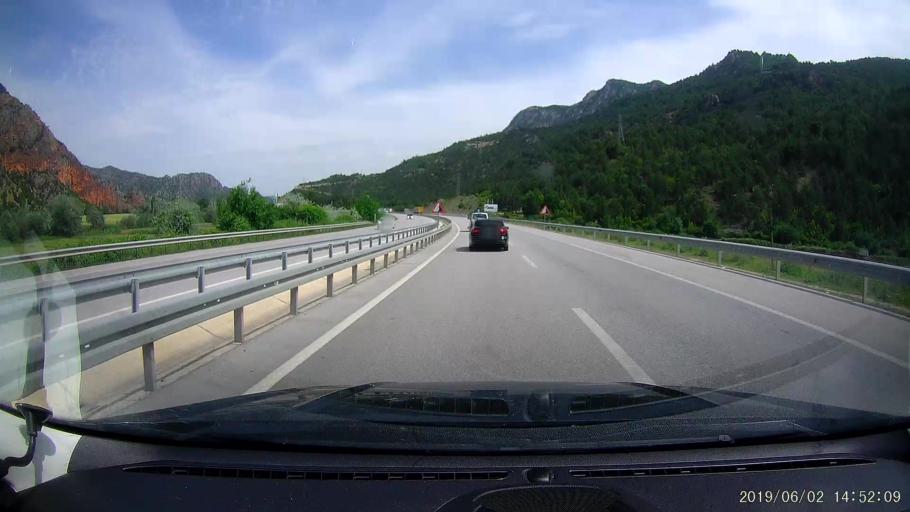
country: TR
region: Corum
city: Hacihamza
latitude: 41.0498
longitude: 34.5489
